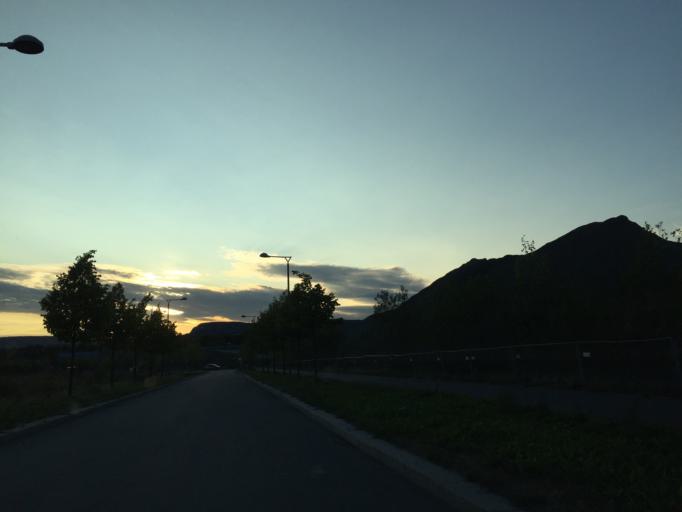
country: NO
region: Akershus
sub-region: Baerum
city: Lysaker
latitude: 59.9002
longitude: 10.6193
